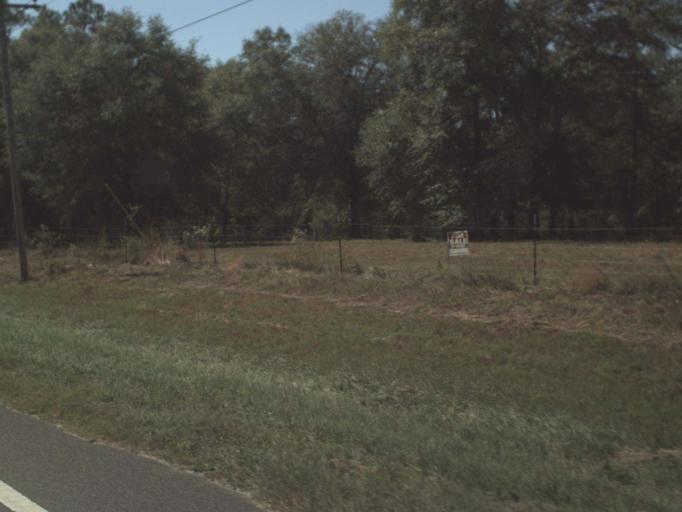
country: US
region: Florida
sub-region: Walton County
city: DeFuniak Springs
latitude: 30.8057
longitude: -86.1235
